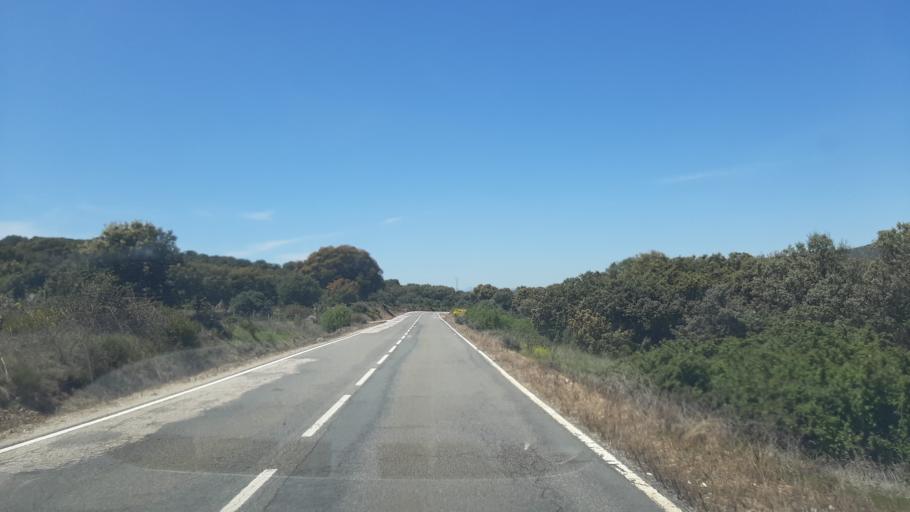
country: ES
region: Castille and Leon
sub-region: Provincia de Avila
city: Narrillos del Alamo
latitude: 40.5330
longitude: -5.4636
